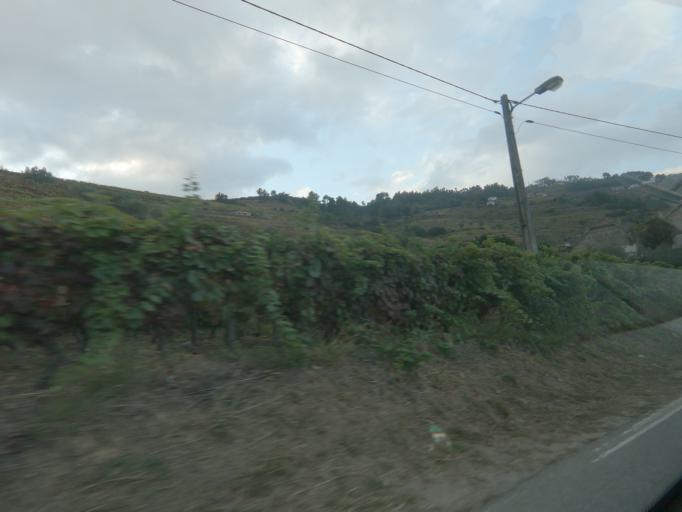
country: PT
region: Vila Real
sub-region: Mesao Frio
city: Mesao Frio
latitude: 41.1696
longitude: -7.8751
